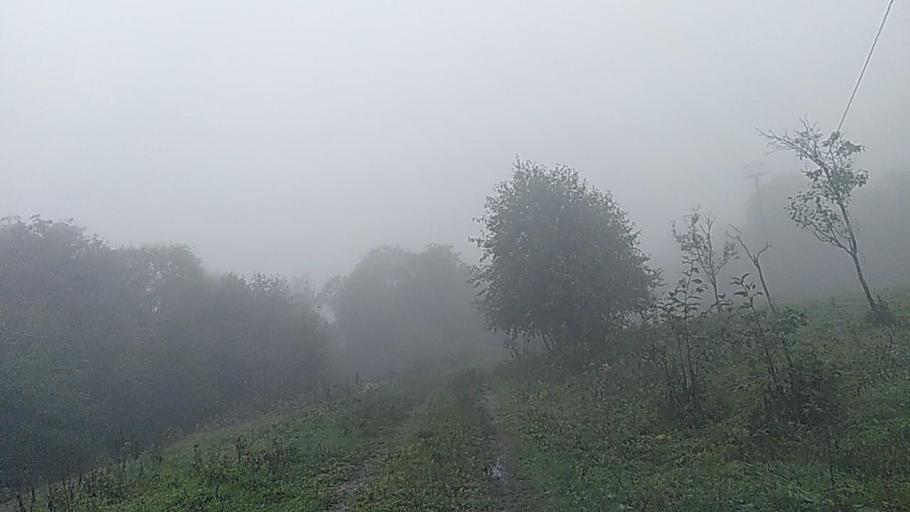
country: RU
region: Kabardino-Balkariya
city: Belaya Rechka
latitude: 43.3566
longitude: 43.3981
